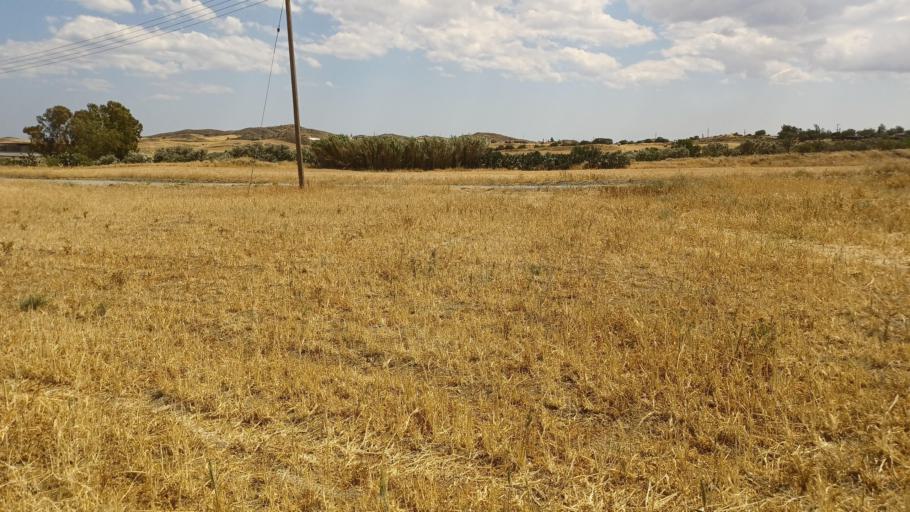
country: CY
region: Larnaka
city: Troulloi
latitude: 35.0187
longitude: 33.6069
